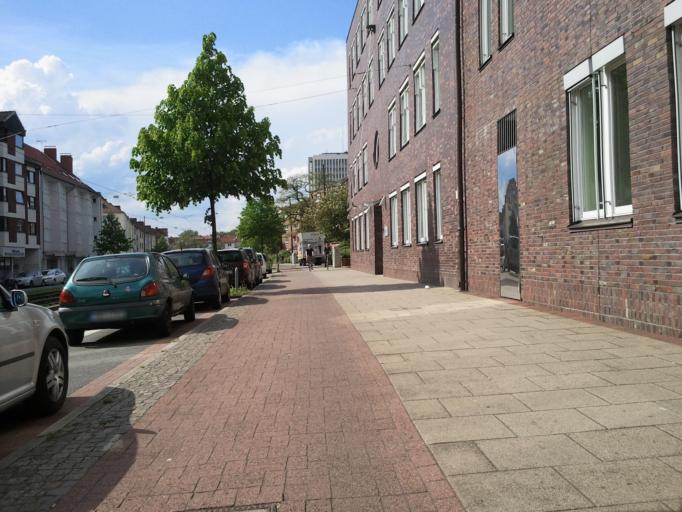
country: DE
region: Bremen
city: Bremen
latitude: 53.0832
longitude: 8.8065
